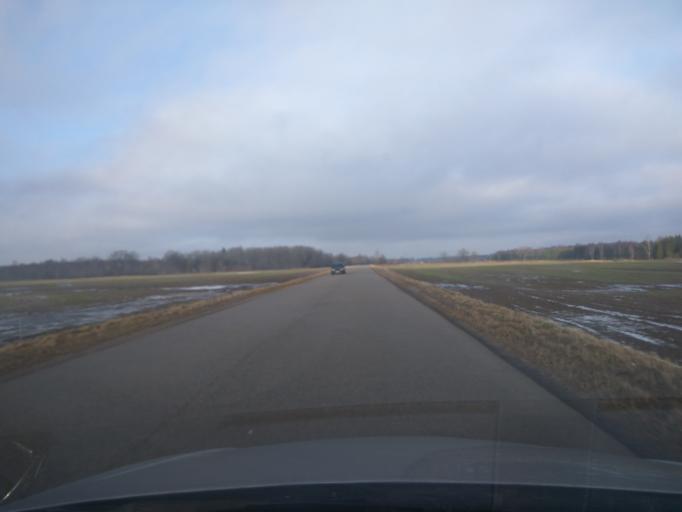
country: LV
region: Saldus Rajons
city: Saldus
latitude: 56.7545
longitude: 22.3867
